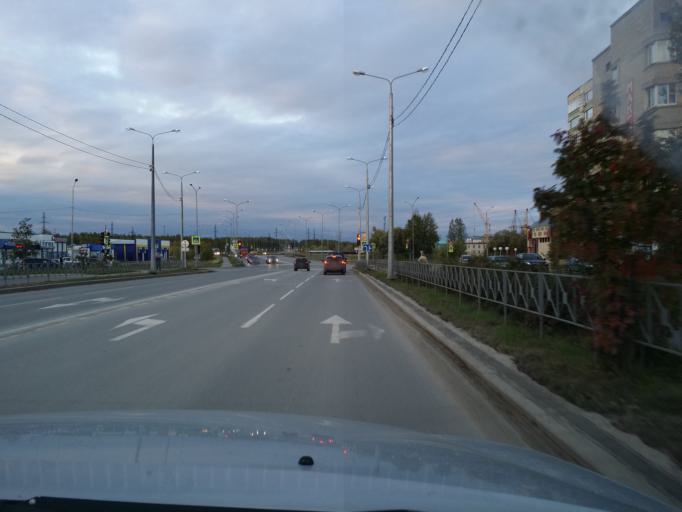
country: RU
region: Khanty-Mansiyskiy Avtonomnyy Okrug
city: Megion
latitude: 61.0404
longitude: 76.1031
